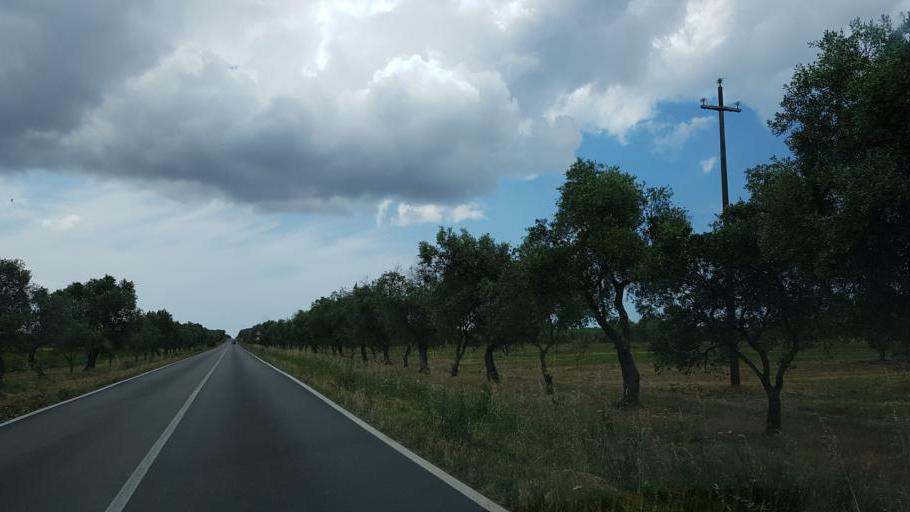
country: IT
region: Apulia
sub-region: Provincia di Brindisi
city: San Pancrazio Salentino
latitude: 40.3742
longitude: 17.8384
